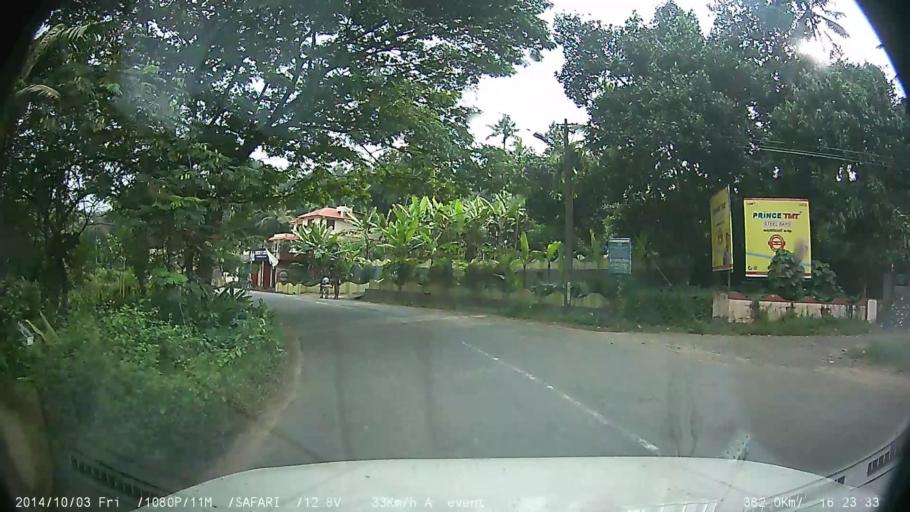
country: IN
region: Kerala
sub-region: Ernakulam
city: Piravam
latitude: 9.8726
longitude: 76.5961
